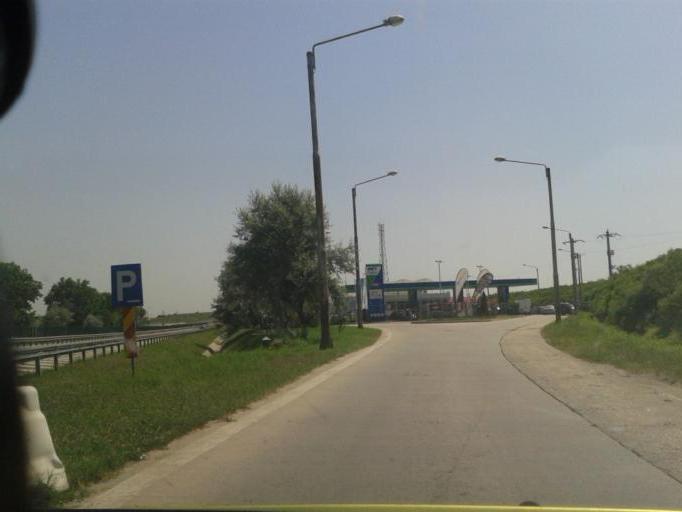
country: RO
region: Calarasi
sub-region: Comuna Sarulesti
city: Sarulesti-Gara
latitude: 44.4423
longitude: 26.6784
